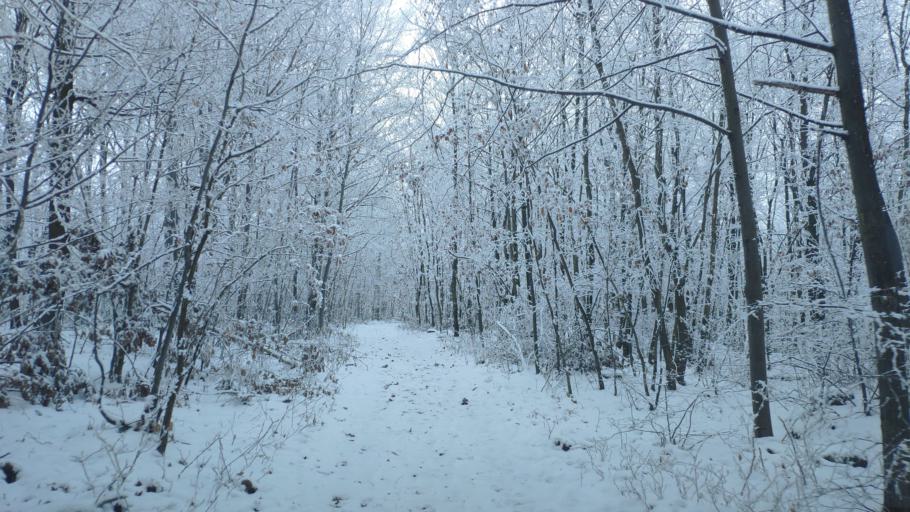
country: SK
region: Kosicky
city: Kosice
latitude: 48.6554
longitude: 21.1842
